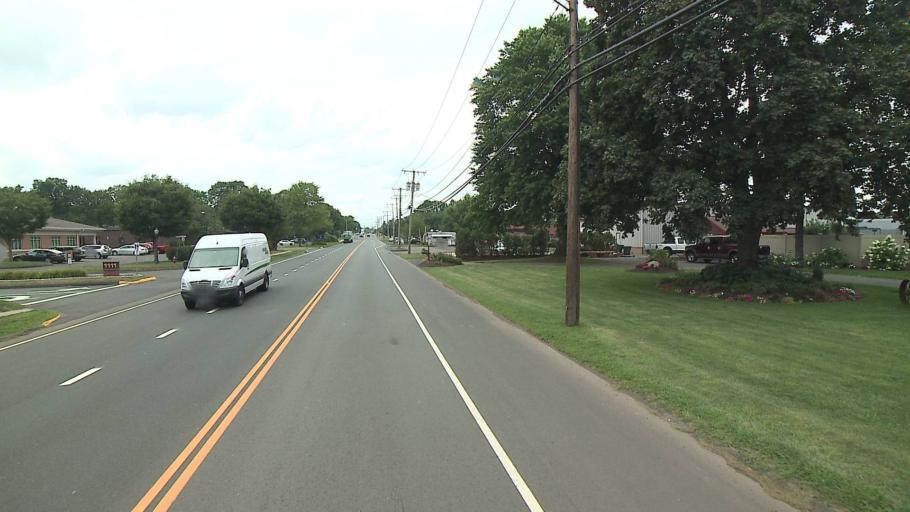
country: US
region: Connecticut
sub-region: Middlesex County
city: Cromwell
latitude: 41.6394
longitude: -72.6764
